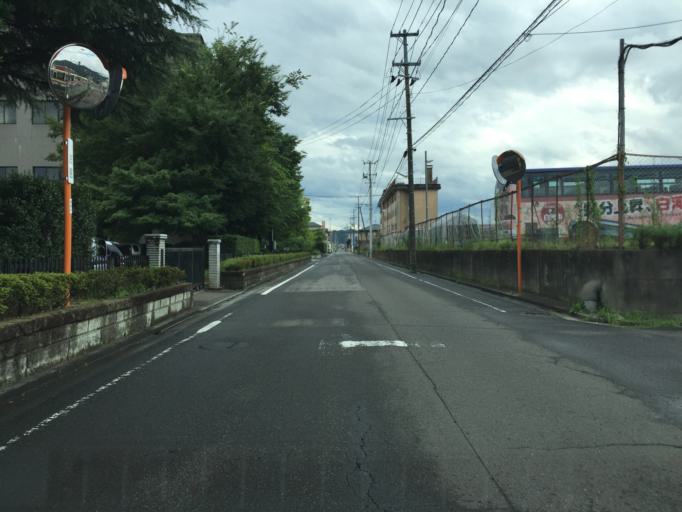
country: JP
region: Fukushima
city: Fukushima-shi
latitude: 37.7653
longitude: 140.4873
